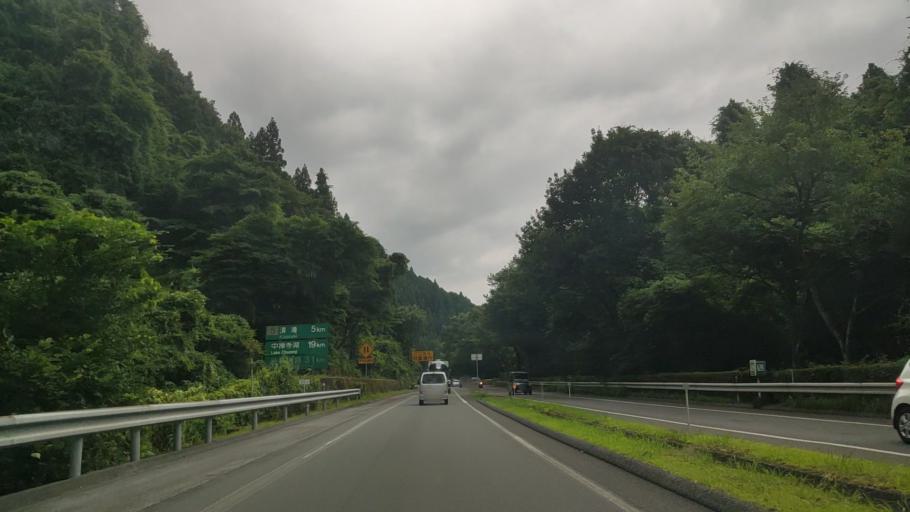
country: JP
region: Tochigi
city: Nikko
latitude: 36.7423
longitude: 139.6210
